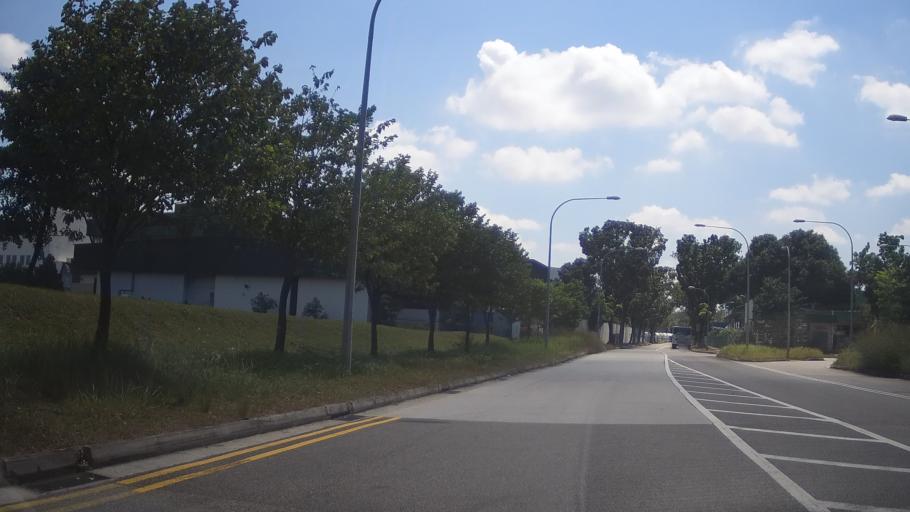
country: SG
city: Singapore
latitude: 1.3149
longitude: 103.7244
